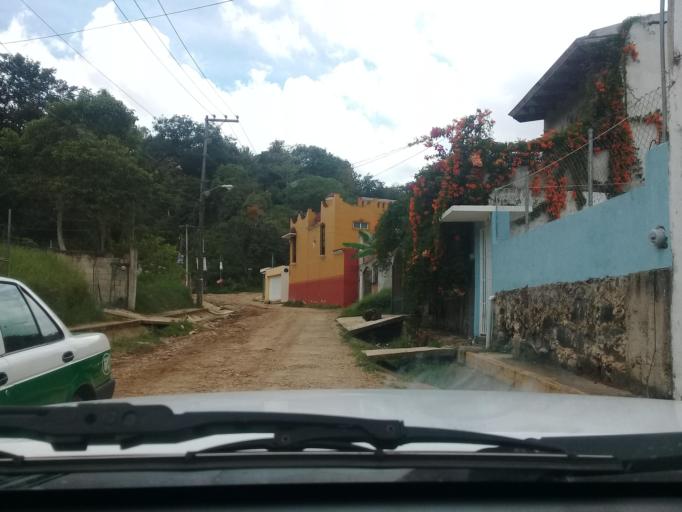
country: MX
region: Veracruz
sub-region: Xalapa
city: Lomas Verdes
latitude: 19.5051
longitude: -96.9100
